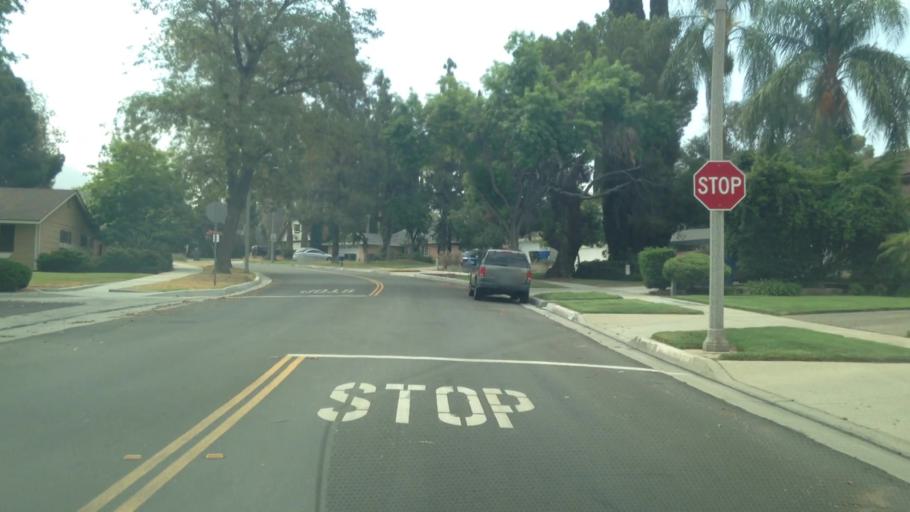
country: US
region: California
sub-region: Riverside County
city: Highgrove
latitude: 33.9895
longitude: -117.3300
